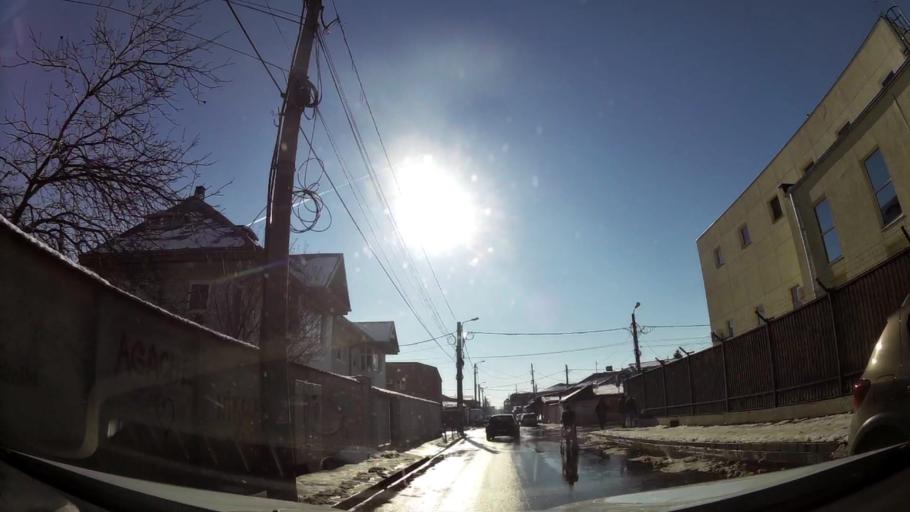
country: RO
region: Bucuresti
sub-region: Municipiul Bucuresti
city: Bucuresti
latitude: 44.4015
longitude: 26.0596
